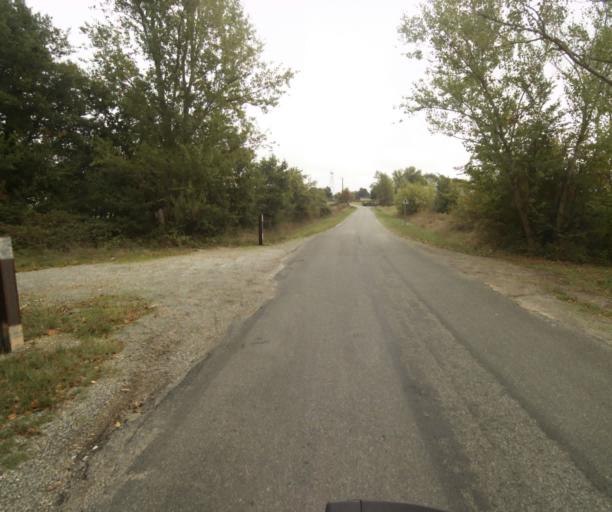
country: FR
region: Midi-Pyrenees
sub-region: Departement du Tarn-et-Garonne
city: Campsas
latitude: 43.9119
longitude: 1.3212
